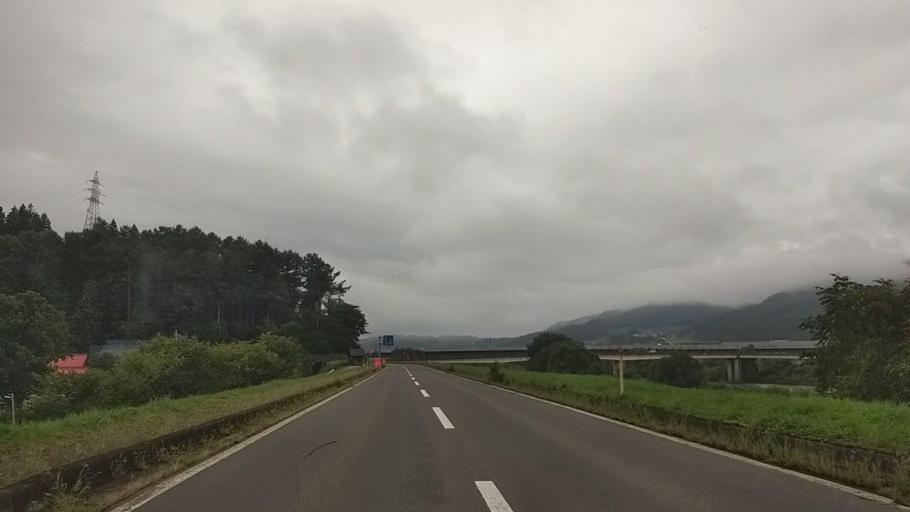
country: JP
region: Nagano
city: Iiyama
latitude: 36.8437
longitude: 138.3680
